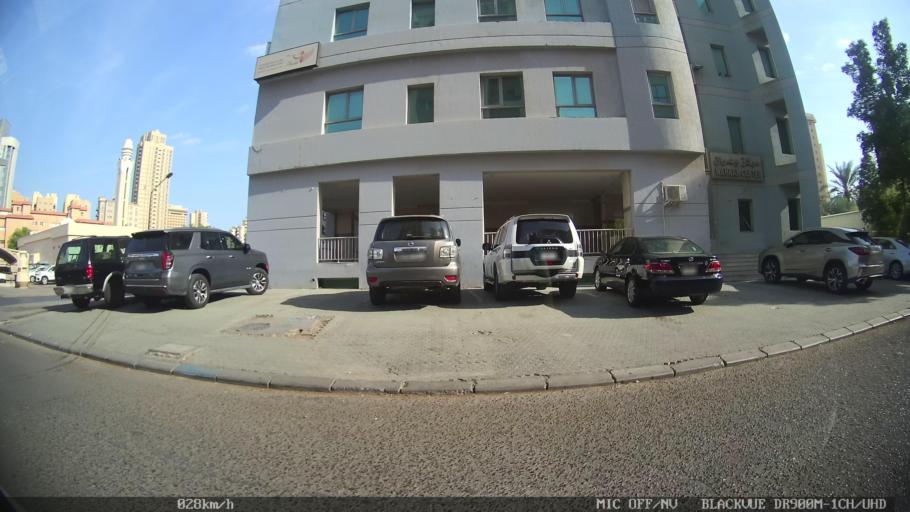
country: KW
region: Al Asimah
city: Ad Dasmah
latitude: 29.3729
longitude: 48.0023
